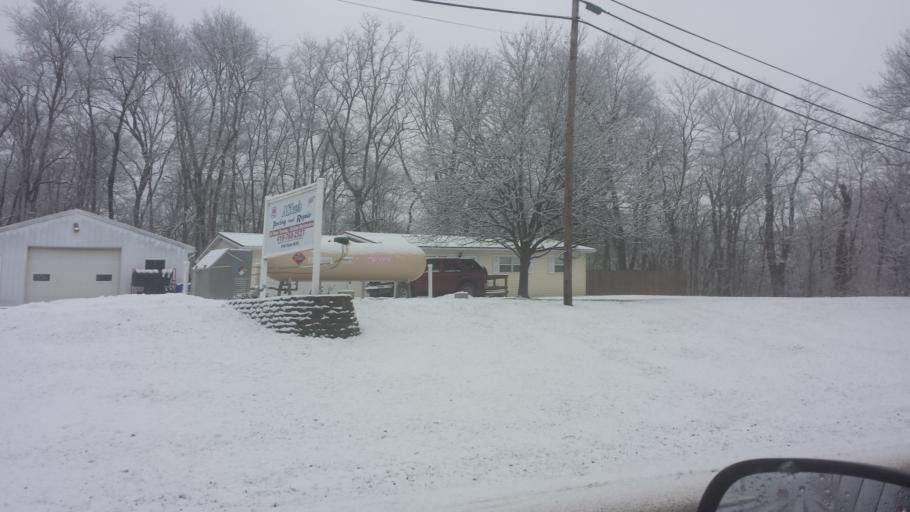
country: US
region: Ohio
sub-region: Knox County
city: Fredericktown
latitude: 40.4809
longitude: -82.6863
